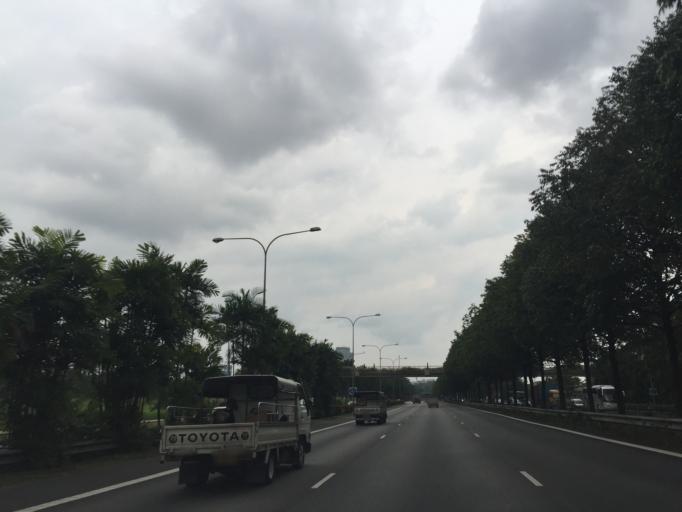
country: SG
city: Singapore
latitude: 1.3252
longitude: 103.7265
